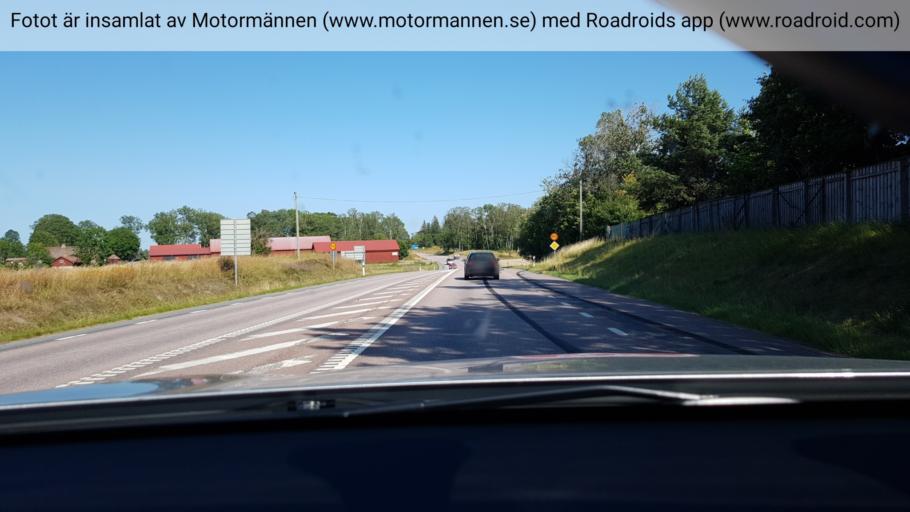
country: SE
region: Uppsala
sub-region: Enkopings Kommun
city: Grillby
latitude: 59.6611
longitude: 17.2464
